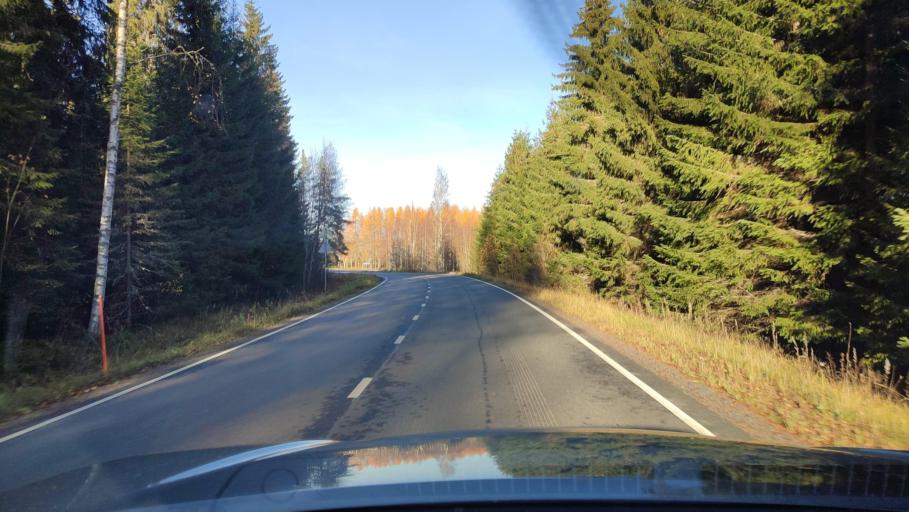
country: FI
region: Southern Ostrobothnia
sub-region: Suupohja
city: Karijoki
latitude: 62.3122
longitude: 21.7038
